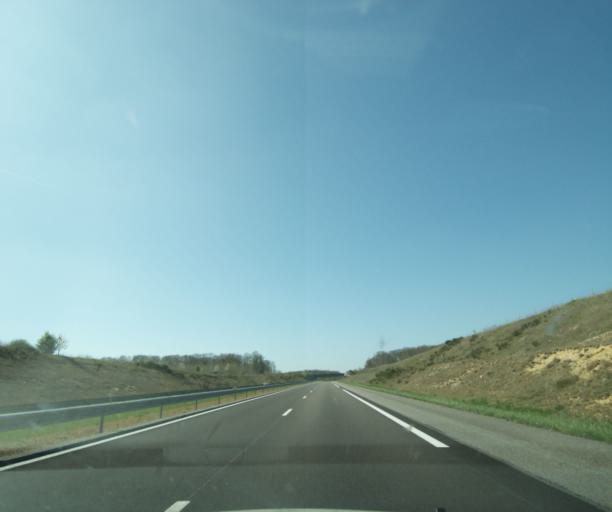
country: FR
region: Centre
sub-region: Departement du Loiret
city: Bonny-sur-Loire
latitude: 47.6102
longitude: 2.8245
